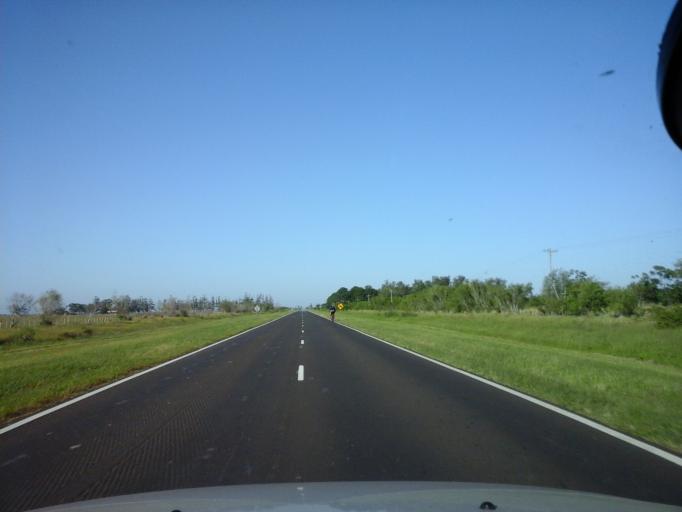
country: AR
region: Corrientes
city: Ita Ibate
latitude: -27.4464
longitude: -57.3931
